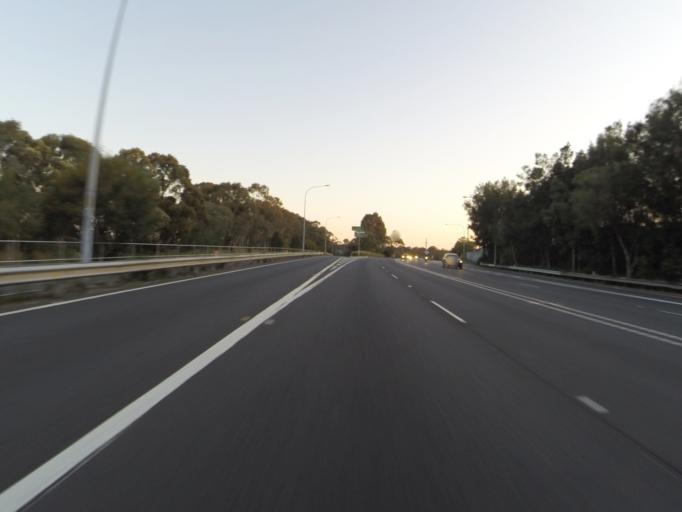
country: AU
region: New South Wales
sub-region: Hurstville
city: Lugarno
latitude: -33.9938
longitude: 151.0269
